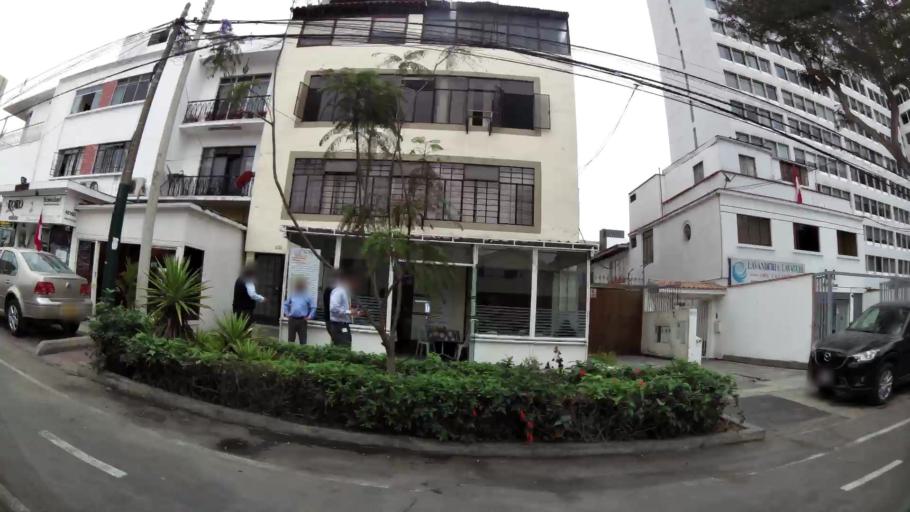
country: PE
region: Lima
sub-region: Lima
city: San Isidro
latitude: -12.0927
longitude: -77.0478
